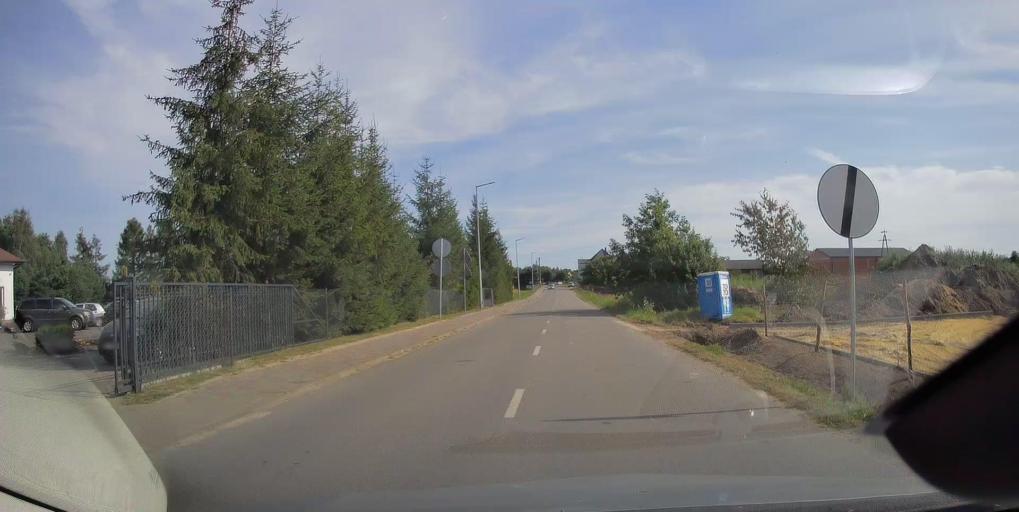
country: PL
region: Lodz Voivodeship
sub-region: Powiat opoczynski
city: Mniszkow
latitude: 51.3723
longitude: 20.0389
